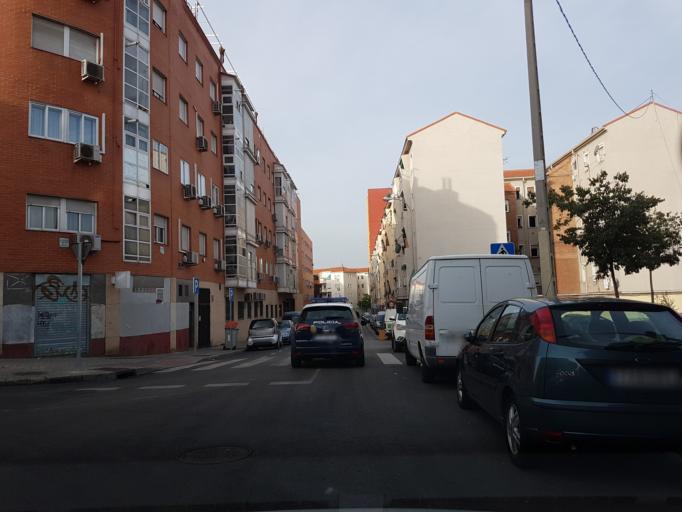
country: ES
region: Madrid
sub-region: Provincia de Madrid
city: Puente de Vallecas
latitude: 40.4038
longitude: -3.6644
